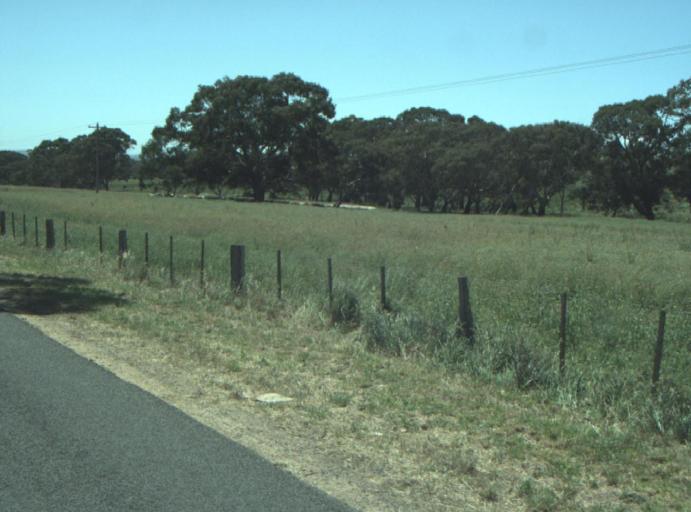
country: AU
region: Victoria
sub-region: Greater Geelong
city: Lara
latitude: -37.8717
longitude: 144.2742
